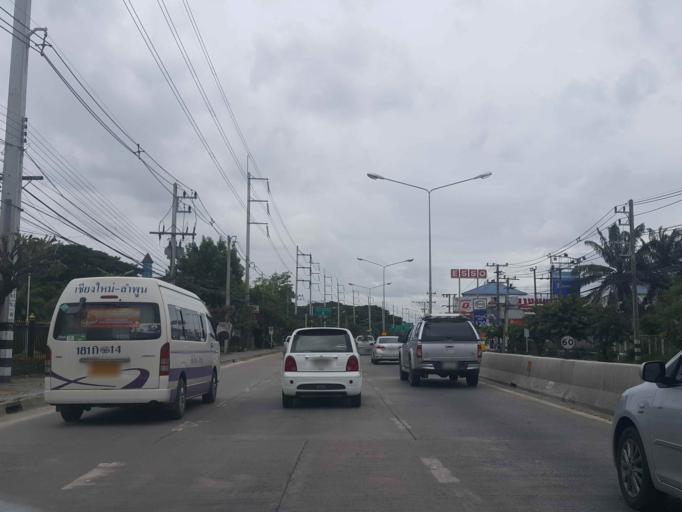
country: TH
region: Chiang Mai
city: Chiang Mai
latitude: 18.7598
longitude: 99.0161
